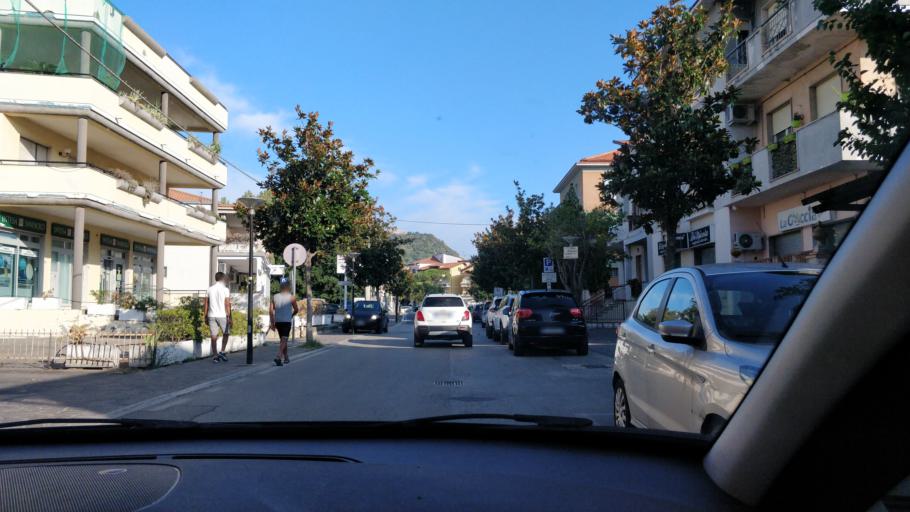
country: IT
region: Abruzzo
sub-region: Provincia di Chieti
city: Sambuceto
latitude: 42.4244
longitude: 14.1857
